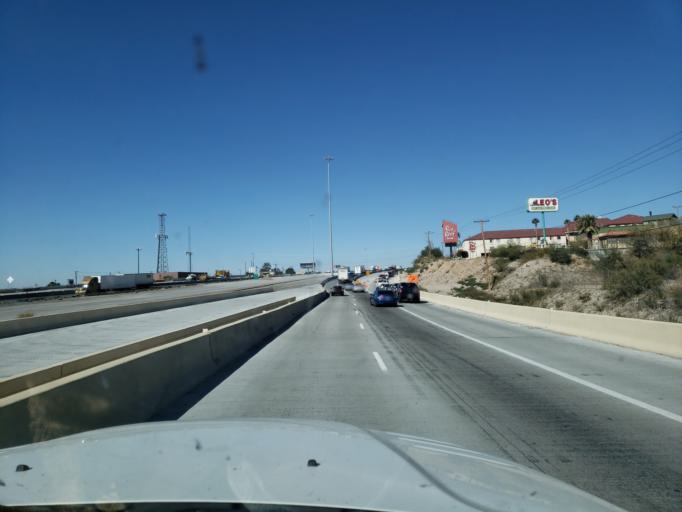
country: US
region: New Mexico
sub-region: Dona Ana County
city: Sunland Park
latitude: 31.8340
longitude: -106.5673
